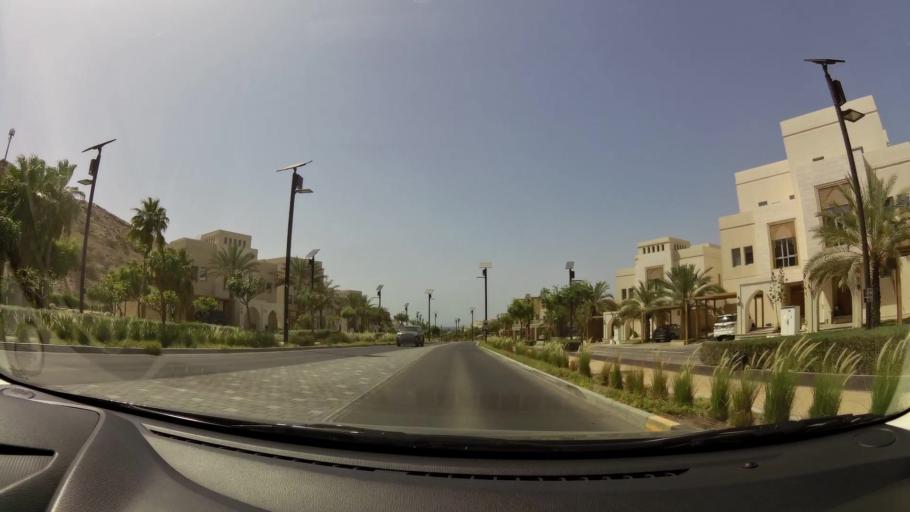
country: OM
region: Muhafazat Masqat
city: Muscat
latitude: 23.6290
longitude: 58.5029
